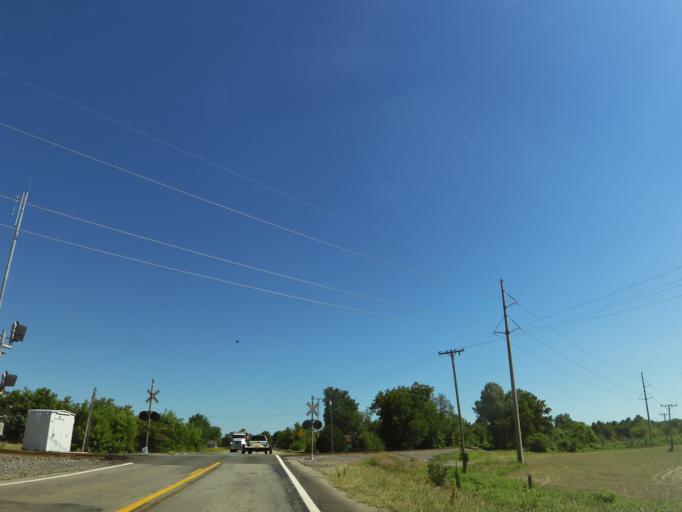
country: US
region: Arkansas
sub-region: Clay County
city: Piggott
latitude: 36.4461
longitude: -90.1472
